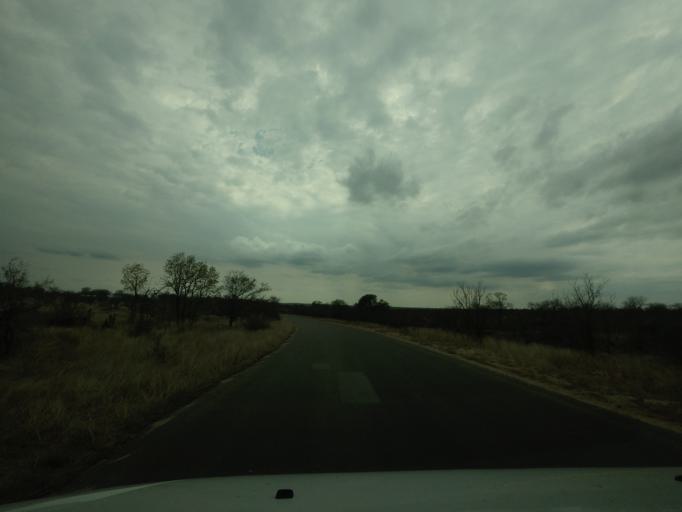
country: ZA
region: Limpopo
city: Thulamahashi
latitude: -24.4799
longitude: 31.3909
